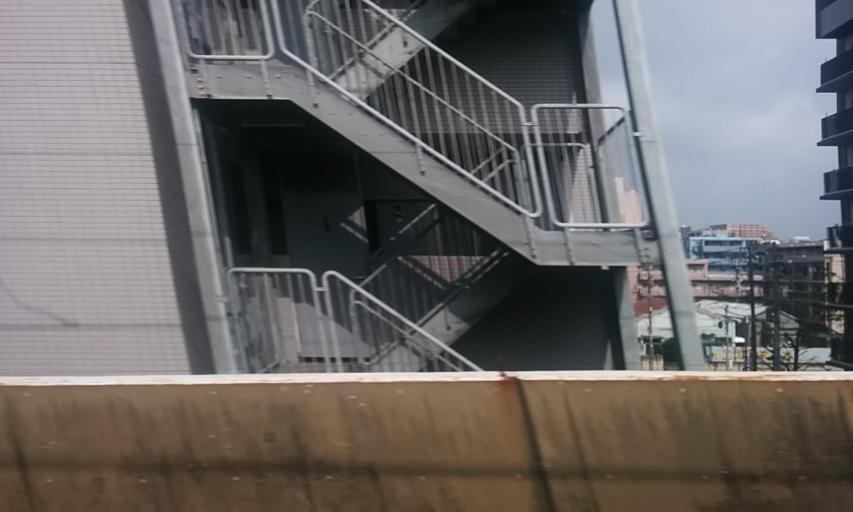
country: JP
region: Kanagawa
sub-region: Kawasaki-shi
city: Kawasaki
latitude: 35.5958
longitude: 139.7377
